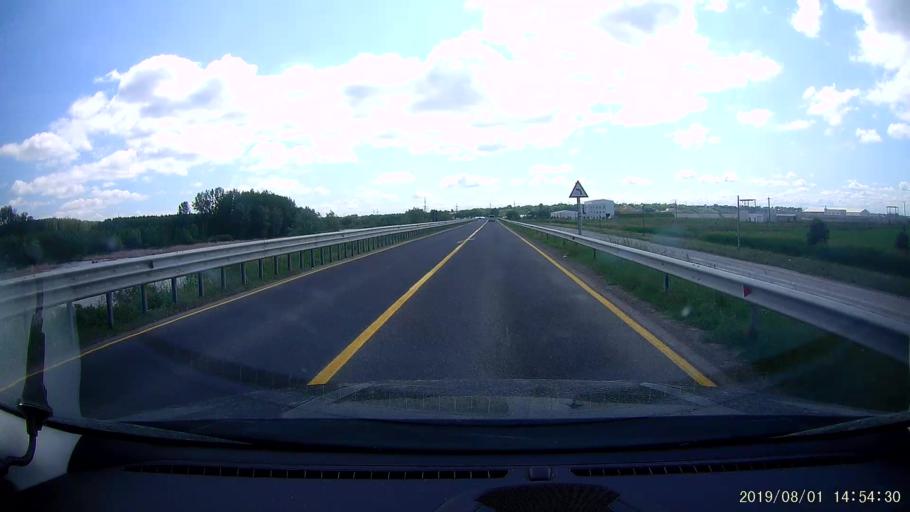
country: RO
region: Braila
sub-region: Municipiul Braila
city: Braila
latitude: 45.3173
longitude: 27.9878
